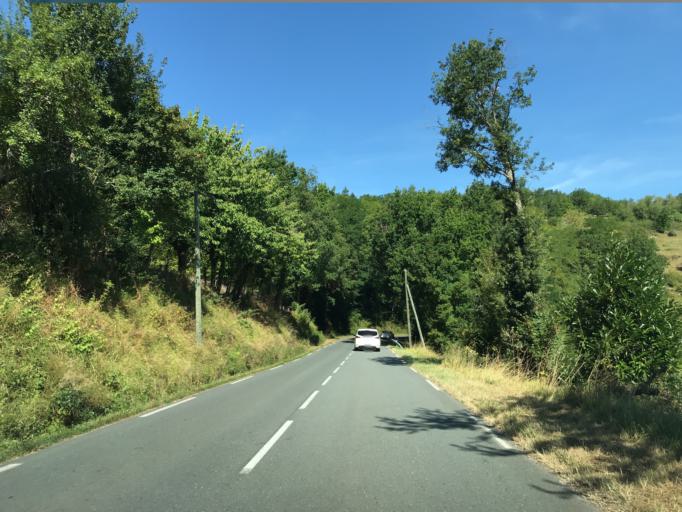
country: FR
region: Limousin
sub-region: Departement de la Correze
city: Larche
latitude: 45.1043
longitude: 1.3855
